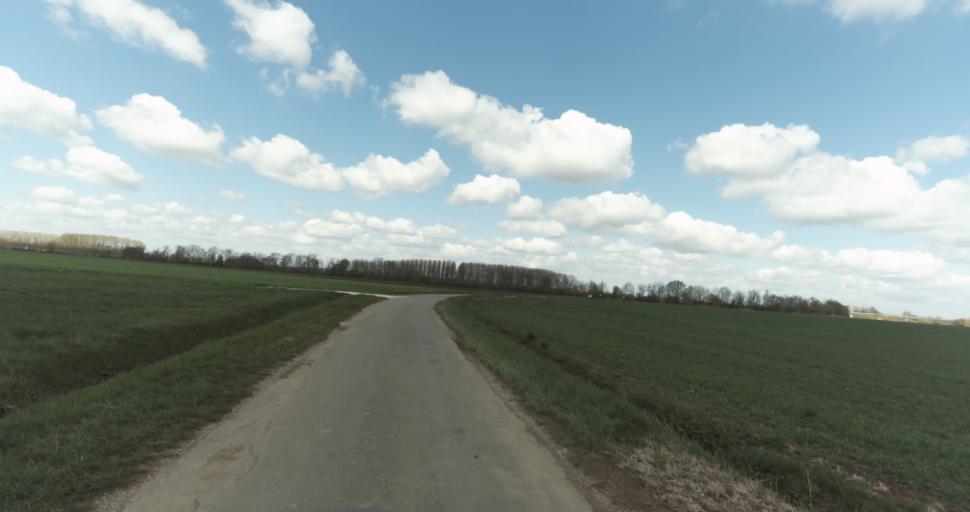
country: FR
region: Bourgogne
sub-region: Departement de la Cote-d'Or
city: Auxonne
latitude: 47.2141
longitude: 5.4038
